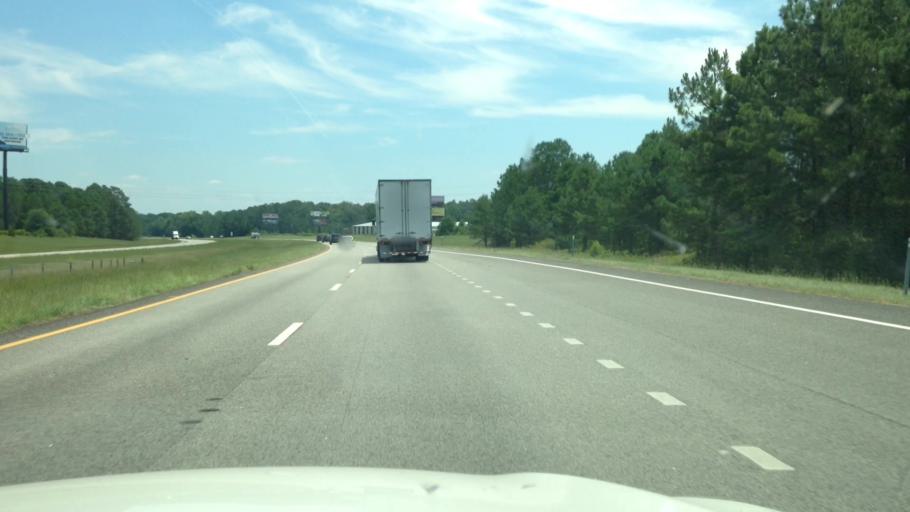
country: US
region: South Carolina
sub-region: Florence County
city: Timmonsville
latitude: 34.2025
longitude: -79.9074
